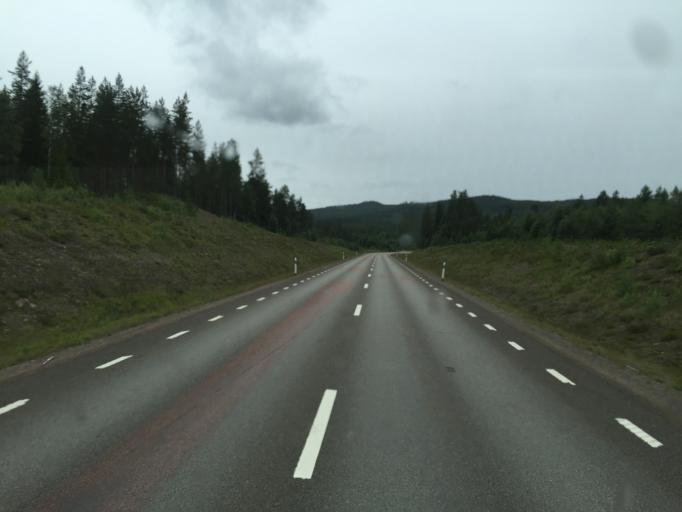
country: SE
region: Dalarna
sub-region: Malung-Saelens kommun
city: Malung
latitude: 60.6072
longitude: 13.5880
